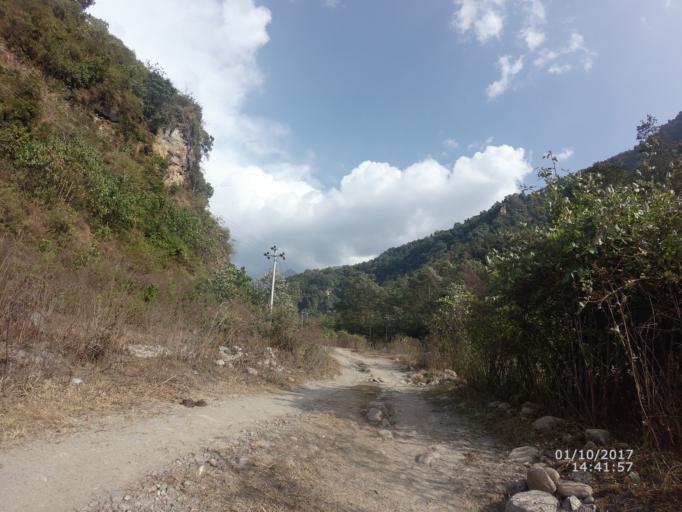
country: NP
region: Western Region
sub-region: Gandaki Zone
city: Pokhara
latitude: 28.3451
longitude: 83.9752
